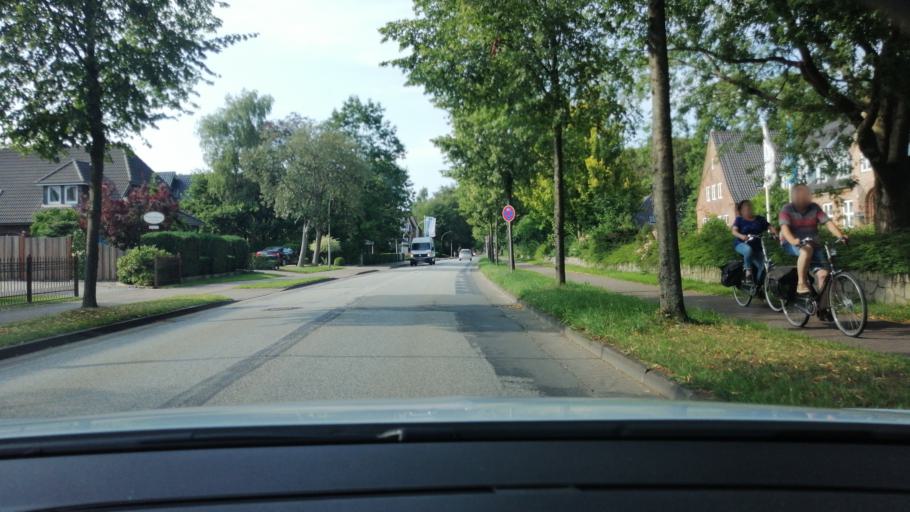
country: DE
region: Schleswig-Holstein
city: Leck
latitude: 54.7667
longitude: 8.9782
